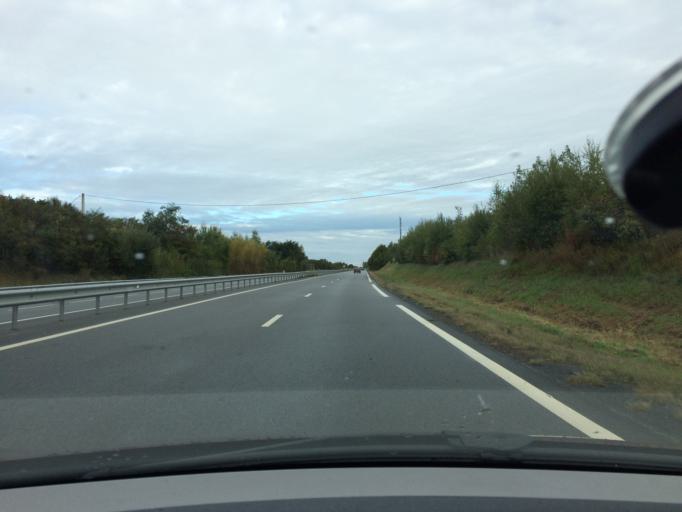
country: FR
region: Brittany
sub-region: Departement d'Ille-et-Vilaine
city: Corps-Nuds
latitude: 47.9807
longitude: -1.5648
